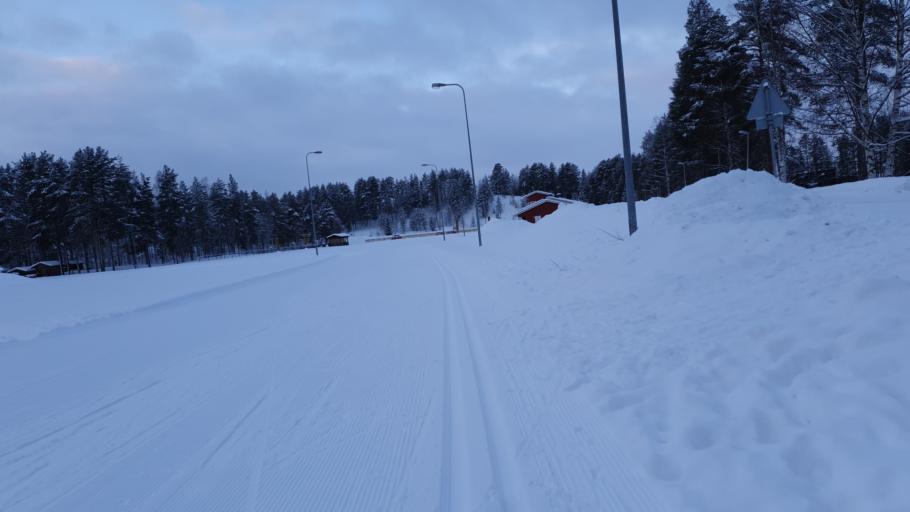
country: FI
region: Kainuu
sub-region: Kehys-Kainuu
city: Kuhmo
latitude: 64.1187
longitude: 29.5856
